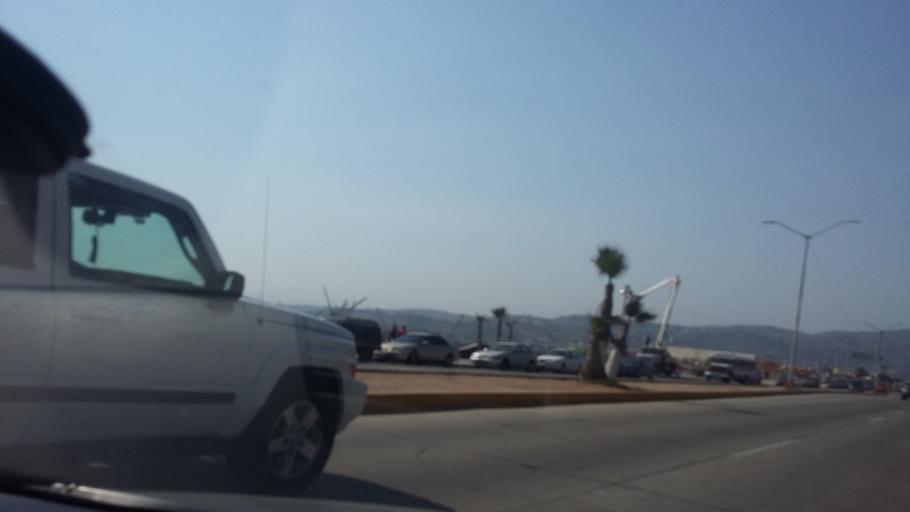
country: MX
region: Baja California
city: Ensenada
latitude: 31.8393
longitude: -116.6107
